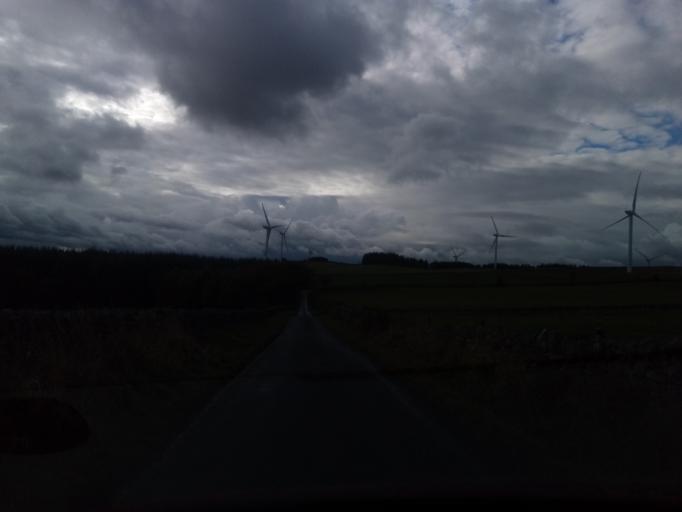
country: GB
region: Scotland
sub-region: The Scottish Borders
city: Galashiels
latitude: 55.6805
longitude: -2.8358
